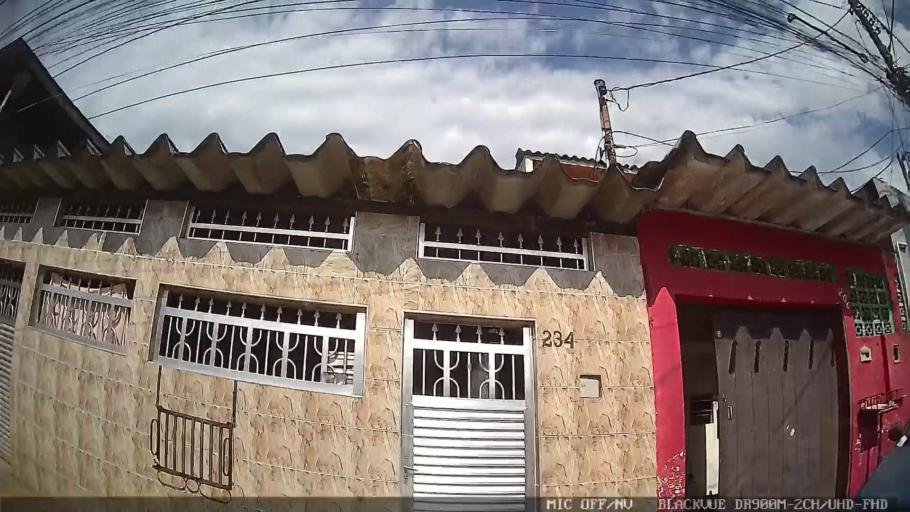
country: BR
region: Sao Paulo
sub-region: Santos
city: Santos
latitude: -23.9456
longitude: -46.2859
